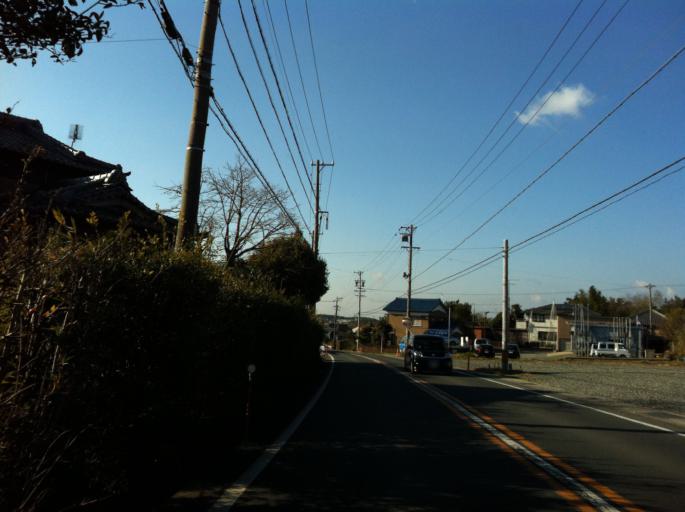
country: JP
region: Aichi
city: Tahara
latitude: 34.6966
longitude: 137.3398
